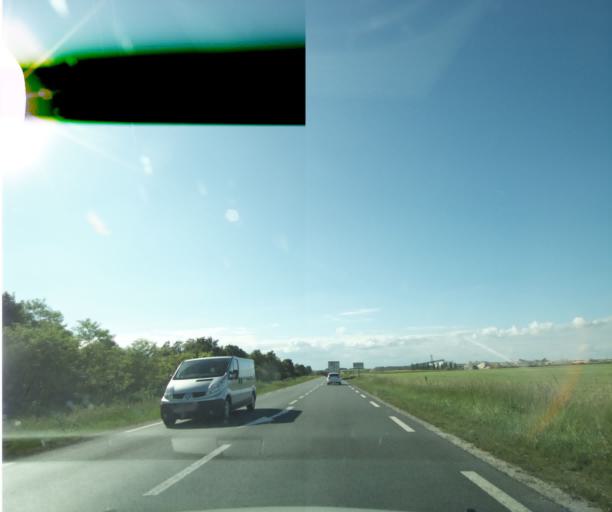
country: FR
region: Centre
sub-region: Departement d'Eure-et-Loir
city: Voves
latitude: 48.2800
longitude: 1.7325
